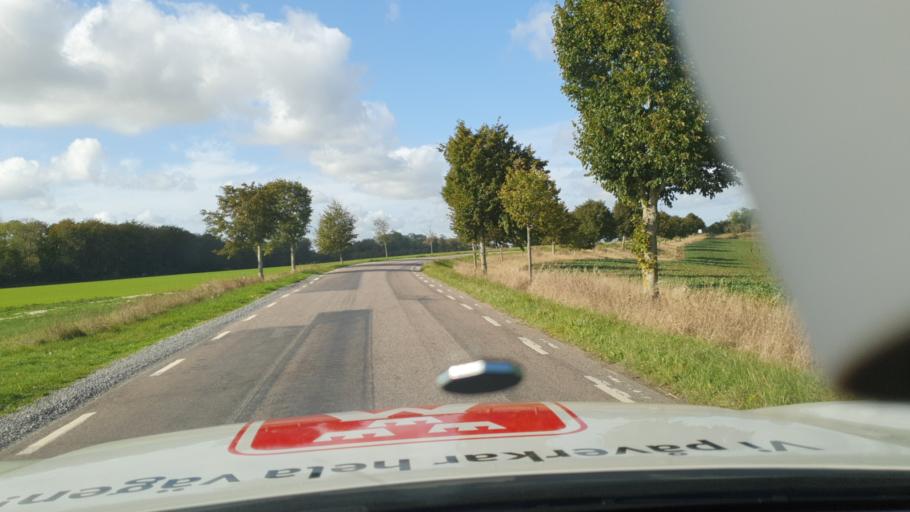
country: SE
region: Skane
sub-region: Ystads Kommun
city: Kopingebro
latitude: 55.4745
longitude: 13.9925
